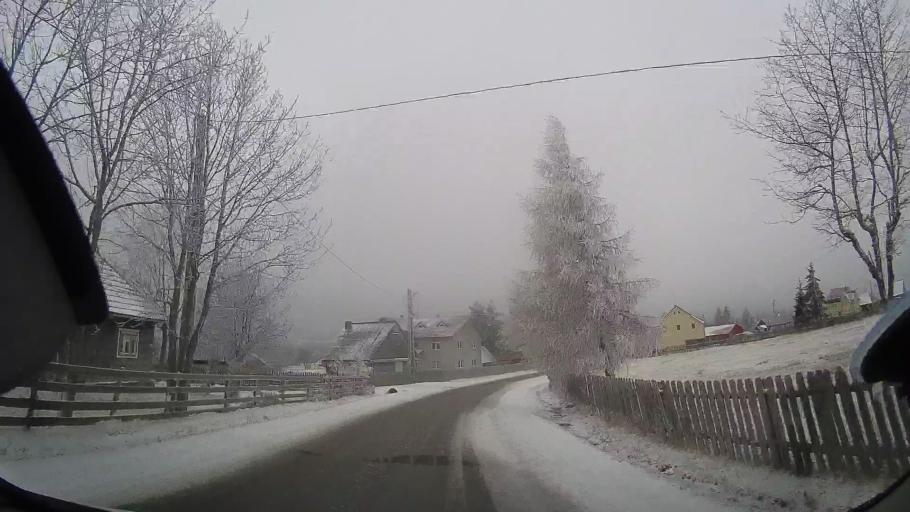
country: RO
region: Cluj
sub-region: Comuna Maguri-Racatau
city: Maguri
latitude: 46.6524
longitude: 23.0824
